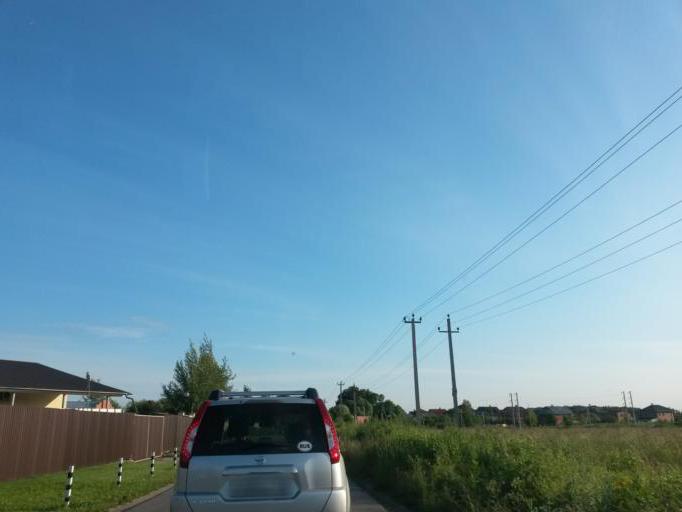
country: RU
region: Moskovskaya
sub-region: Podol'skiy Rayon
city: Podol'sk
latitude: 55.3964
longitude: 37.6211
